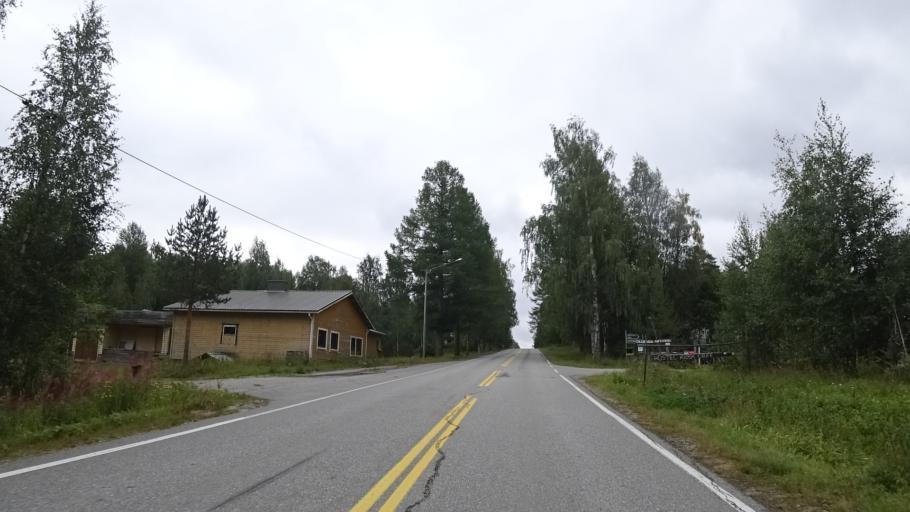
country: FI
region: North Karelia
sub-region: Pielisen Karjala
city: Lieksa
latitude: 63.2847
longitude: 30.5279
